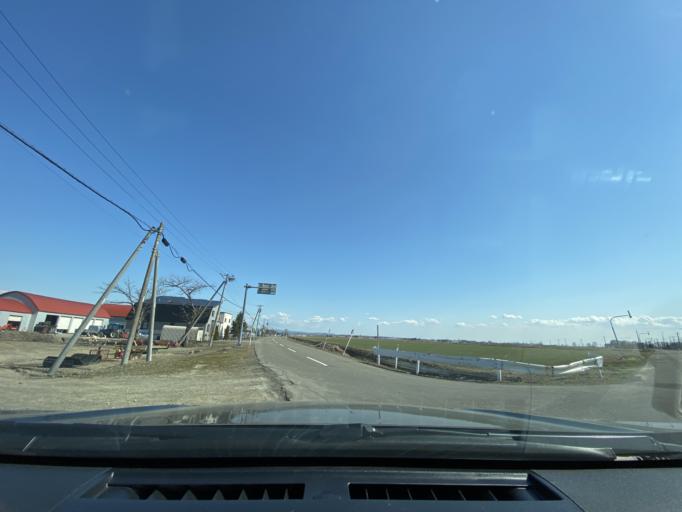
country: JP
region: Hokkaido
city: Iwamizawa
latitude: 43.2932
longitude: 141.6813
